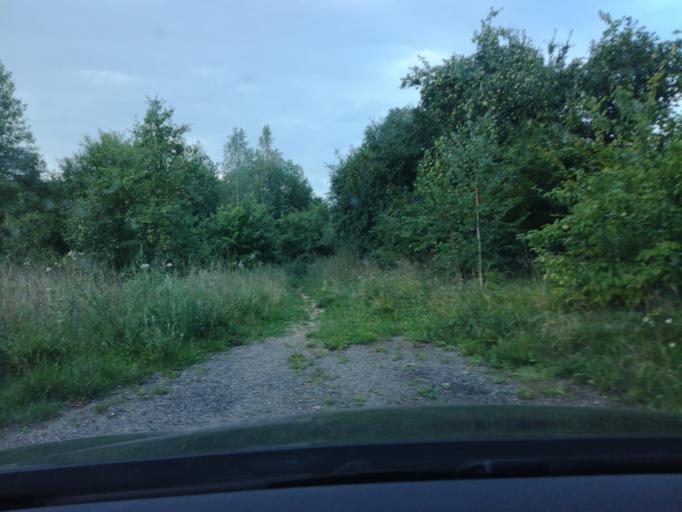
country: LT
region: Alytaus apskritis
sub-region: Alytus
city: Alytus
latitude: 54.3919
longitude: 24.0138
